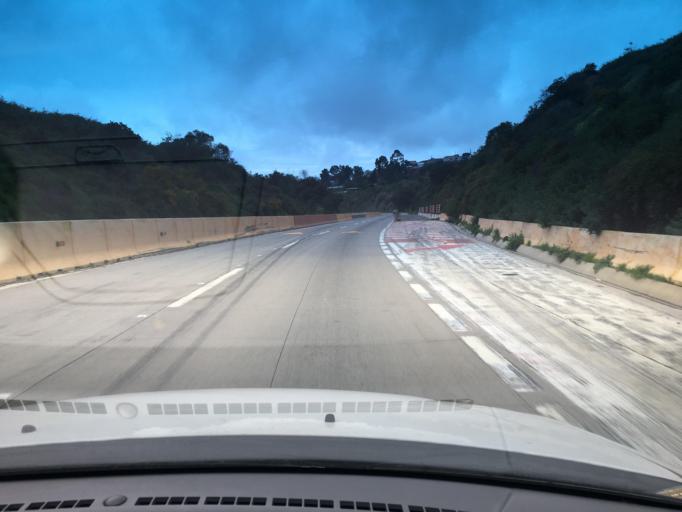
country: CL
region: Valparaiso
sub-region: Provincia de Valparaiso
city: Valparaiso
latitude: -33.0652
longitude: -71.6424
